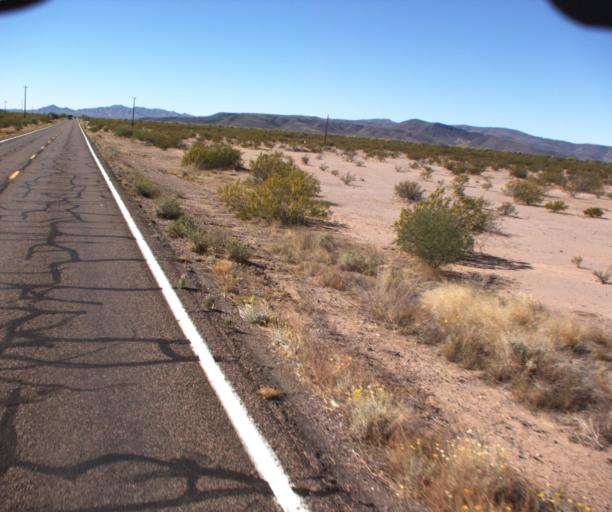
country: US
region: Arizona
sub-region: Pima County
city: Ajo
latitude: 32.5303
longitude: -112.8803
